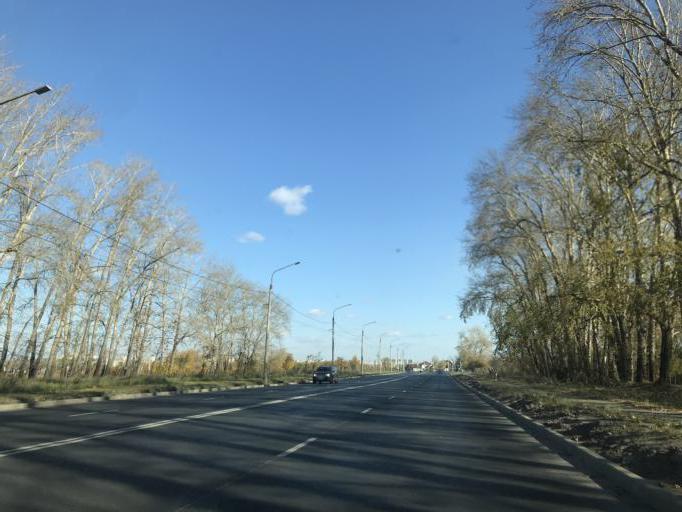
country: RU
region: Chelyabinsk
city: Roshchino
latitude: 55.2400
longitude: 61.3392
